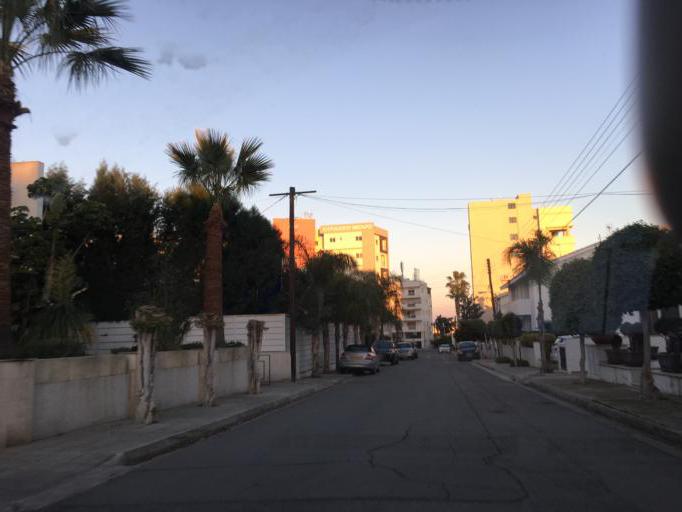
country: CY
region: Larnaka
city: Larnaca
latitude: 34.9074
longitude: 33.6280
